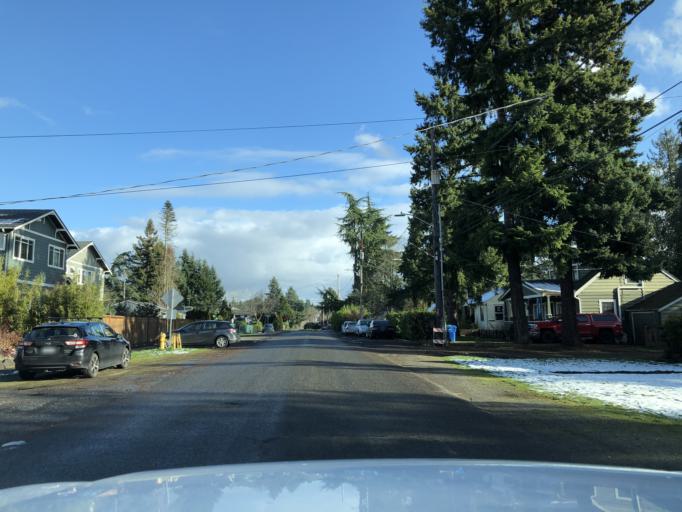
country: US
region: Washington
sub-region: King County
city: Lake Forest Park
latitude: 47.7212
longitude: -122.3034
